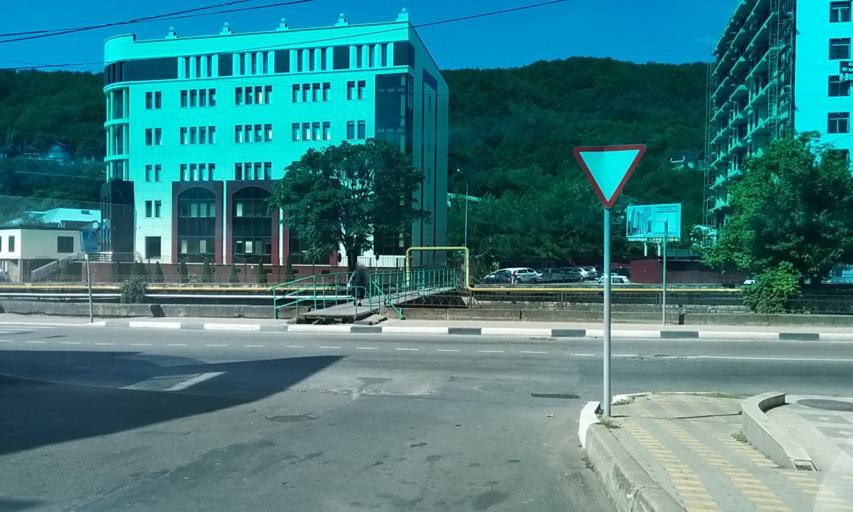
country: RU
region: Krasnodarskiy
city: Tuapse
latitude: 44.1030
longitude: 39.0586
